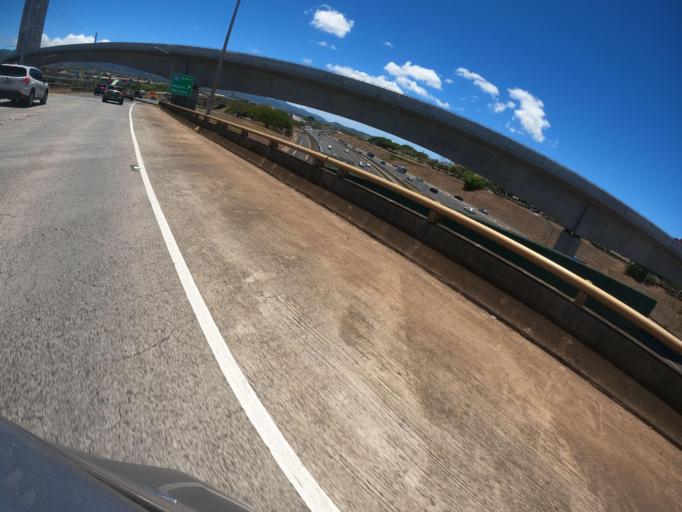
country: US
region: Hawaii
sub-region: Honolulu County
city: Pearl City, Manana
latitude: 21.3968
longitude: -157.9830
